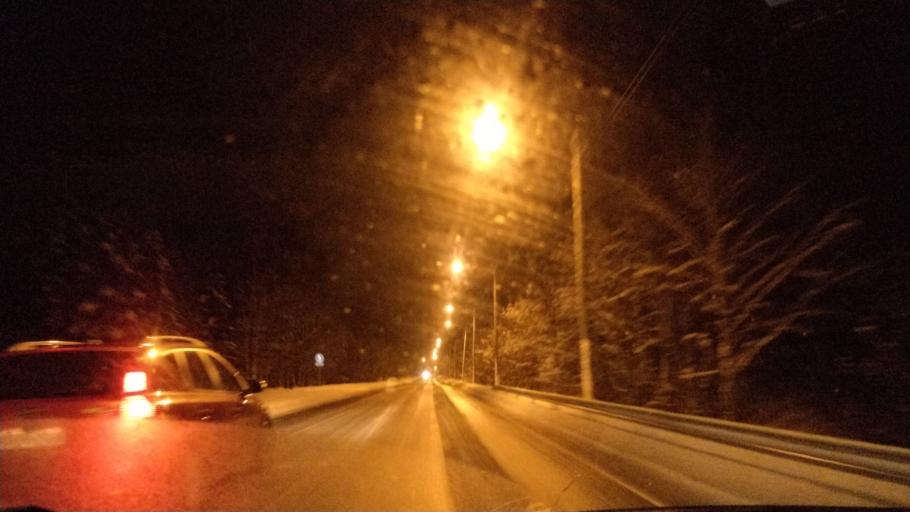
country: FI
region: Lapland
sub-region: Rovaniemi
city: Rovaniemi
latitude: 66.2661
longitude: 25.3346
